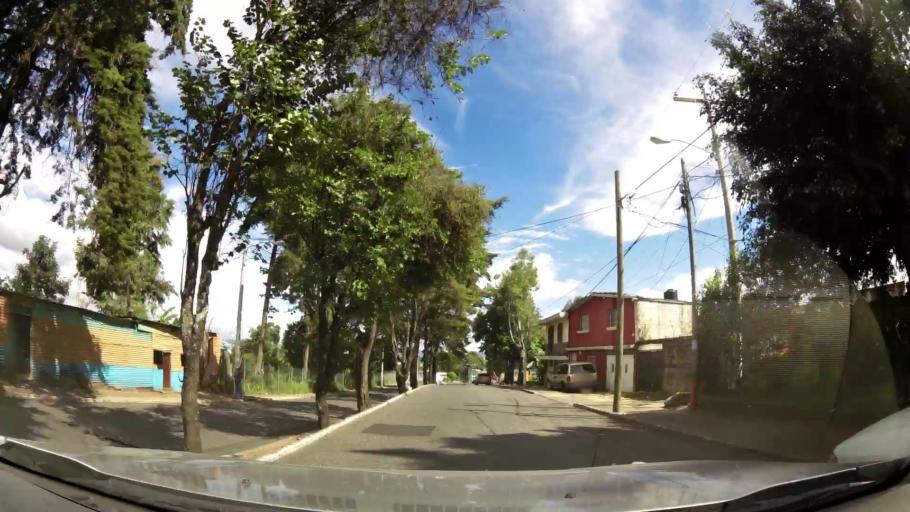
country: GT
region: Guatemala
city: Mixco
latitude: 14.6744
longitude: -90.5683
